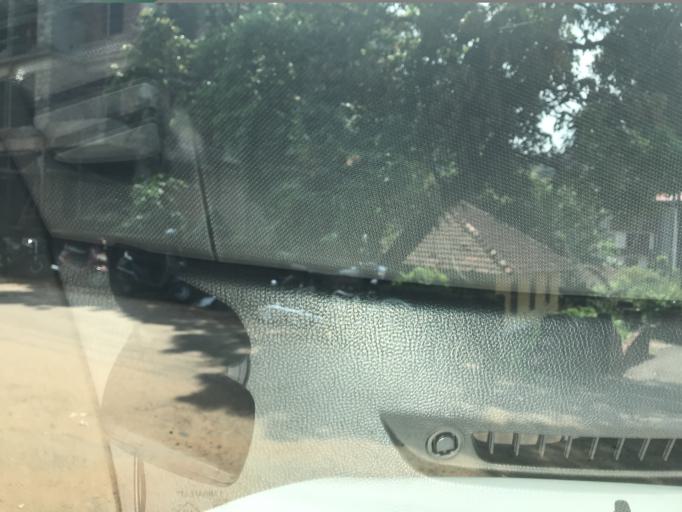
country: IN
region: Karnataka
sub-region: Dakshina Kannada
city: Mangalore
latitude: 12.8777
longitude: 74.8433
